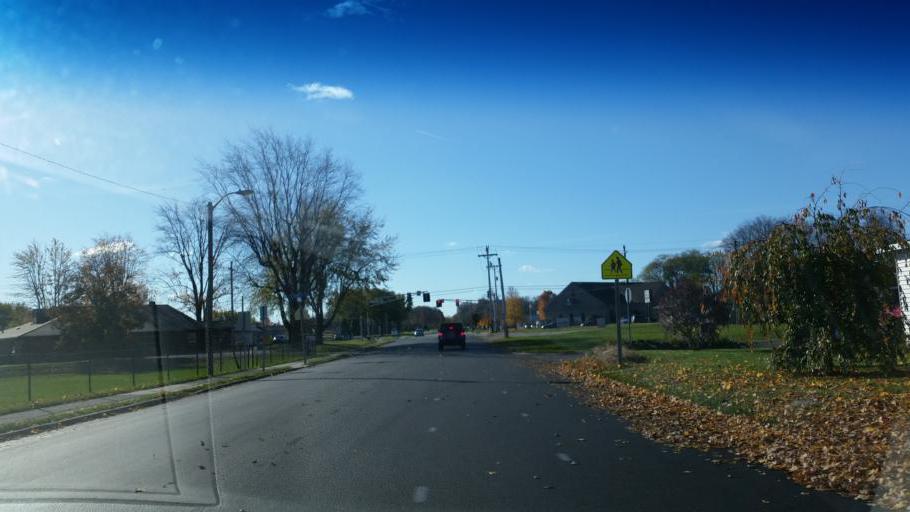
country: US
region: Indiana
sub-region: Howard County
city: Kokomo
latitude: 40.4562
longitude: -86.1365
